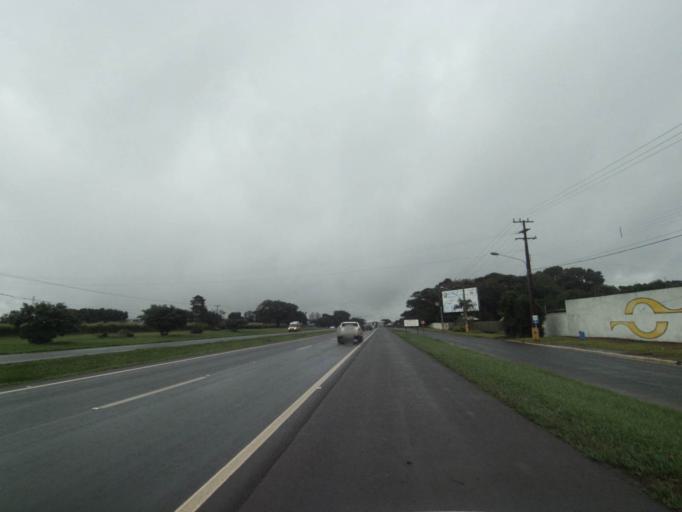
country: BR
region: Parana
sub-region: Foz Do Iguacu
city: Foz do Iguacu
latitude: -25.5102
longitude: -54.5612
